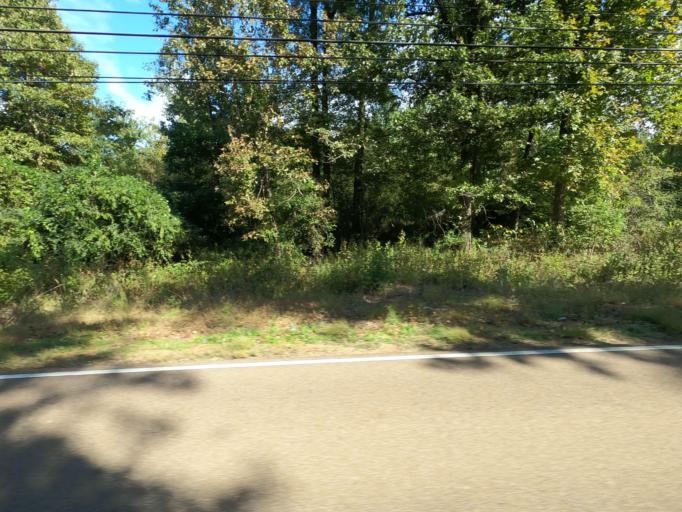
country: US
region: Tennessee
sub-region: Fayette County
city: Hickory Withe
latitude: 35.2241
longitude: -89.6503
